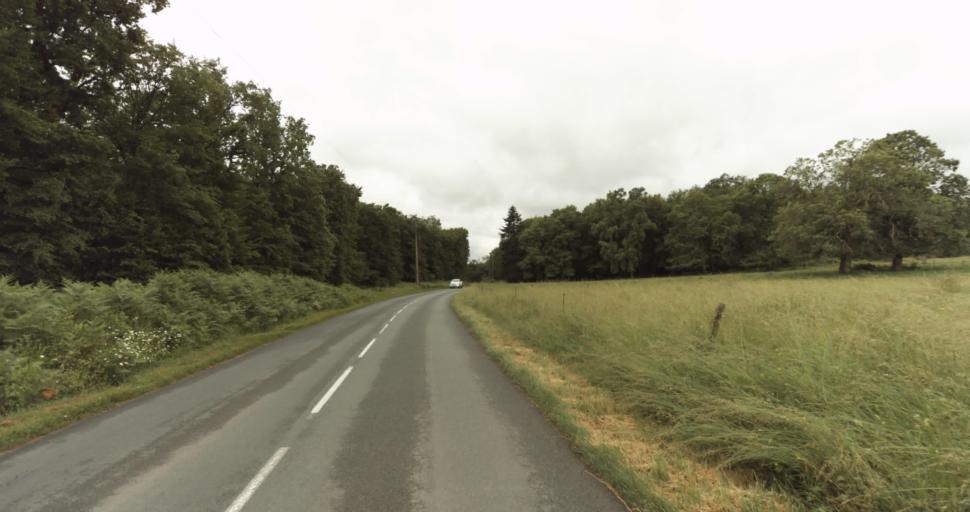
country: FR
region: Aquitaine
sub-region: Departement de la Dordogne
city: Belves
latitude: 44.6934
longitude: 0.9116
